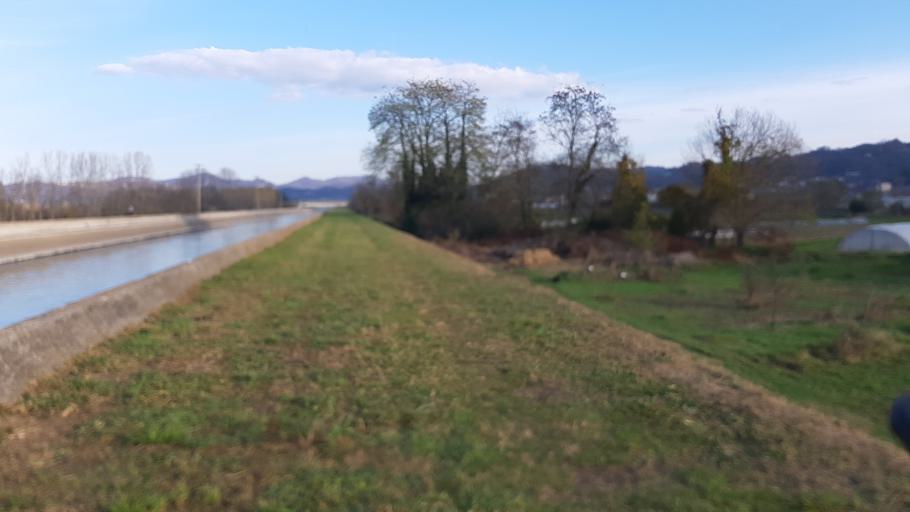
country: IT
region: Piedmont
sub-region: Provincia di Torino
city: San Mauro Torinese
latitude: 45.1224
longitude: 7.7831
